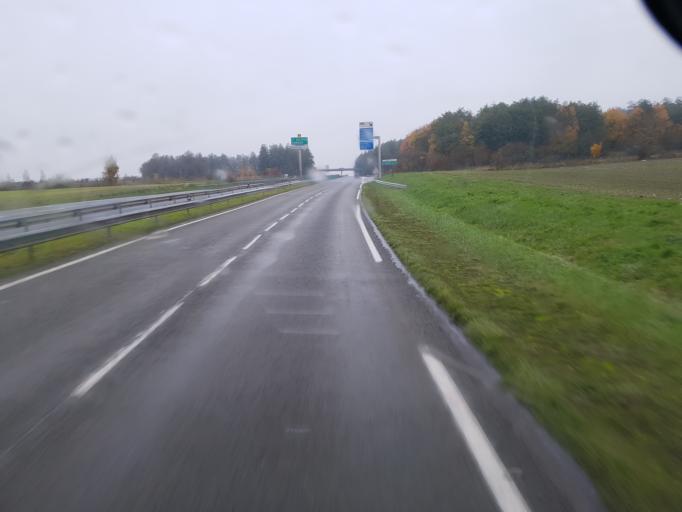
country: FR
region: Picardie
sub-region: Departement de l'Aisne
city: Gauchy
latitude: 49.8112
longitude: 3.2876
